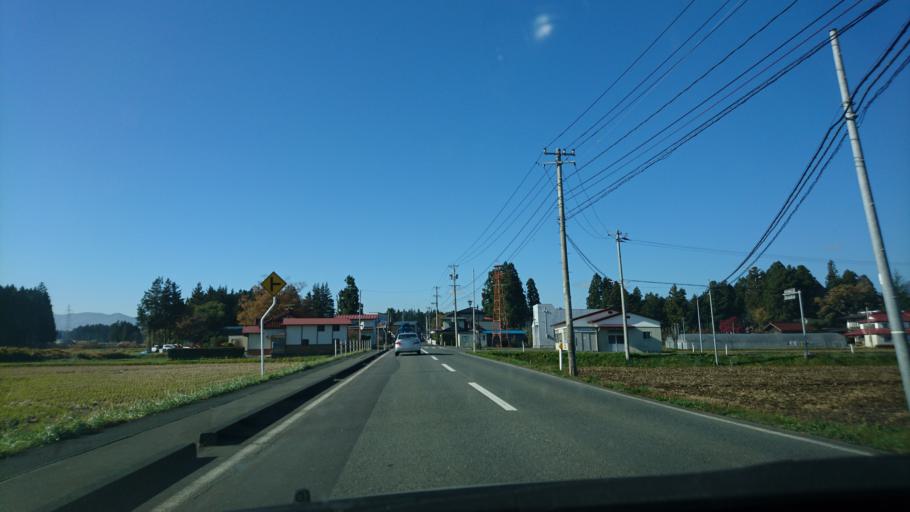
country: JP
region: Iwate
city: Mizusawa
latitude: 39.1305
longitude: 141.0433
